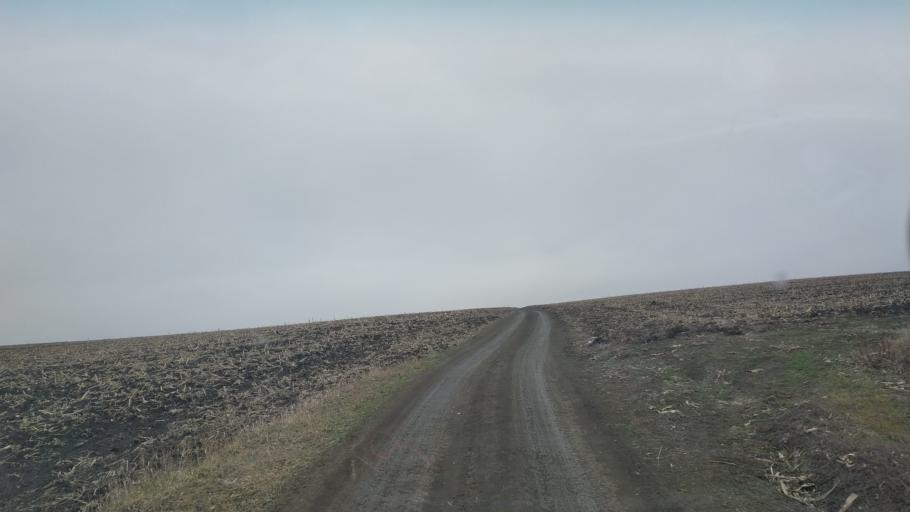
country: MD
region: Chisinau
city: Singera
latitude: 46.8279
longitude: 29.0031
